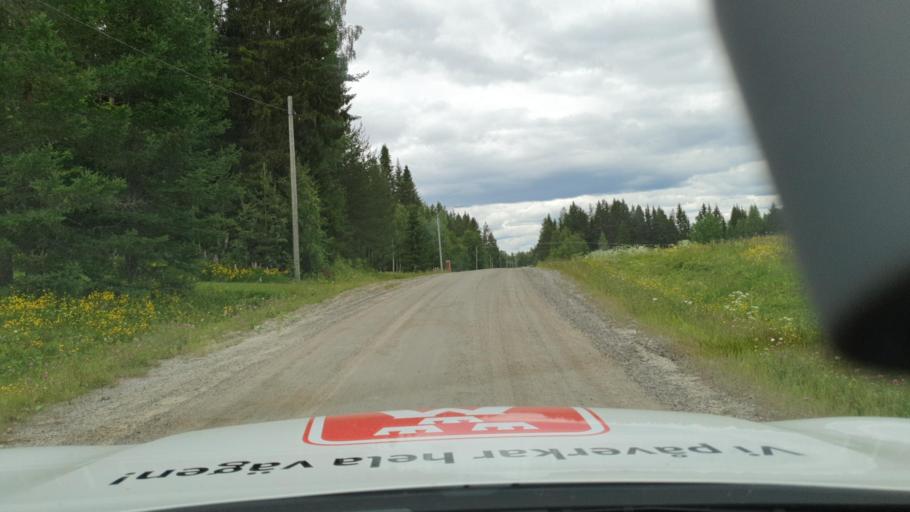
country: SE
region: Vaesterbotten
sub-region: Bjurholms Kommun
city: Bjurholm
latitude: 63.7431
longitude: 19.2779
